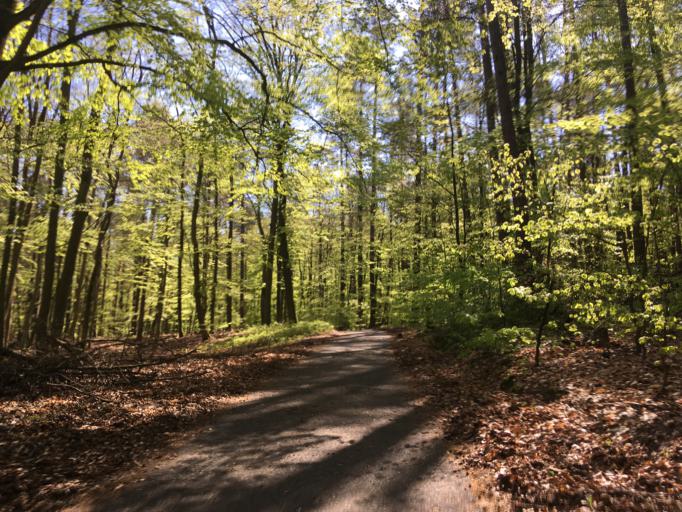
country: DE
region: Brandenburg
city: Wandlitz
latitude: 52.7398
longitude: 13.4966
